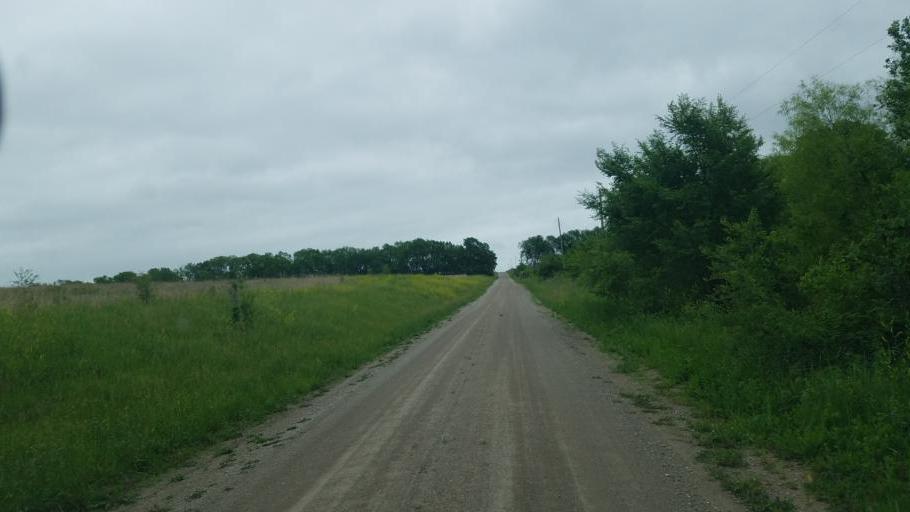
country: US
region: Missouri
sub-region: Carroll County
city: Carrollton
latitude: 39.4852
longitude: -93.5073
